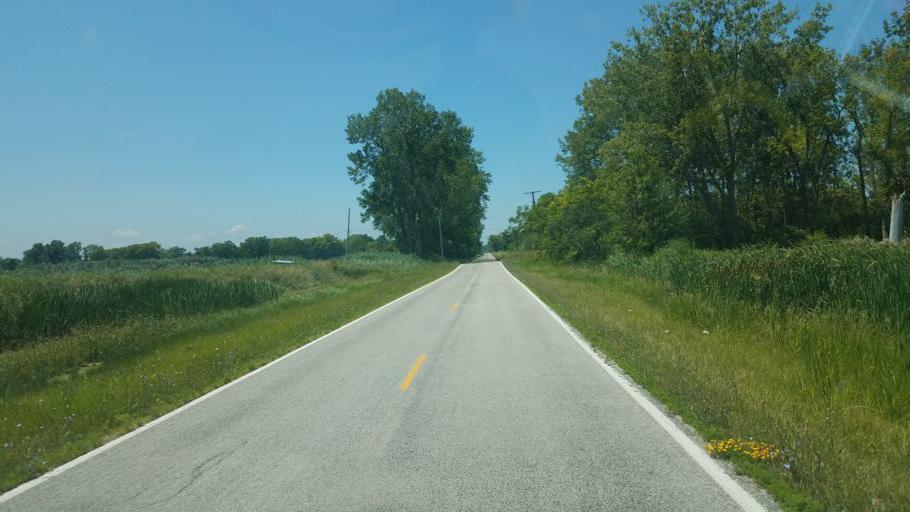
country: US
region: Ohio
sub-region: Ottawa County
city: Port Clinton
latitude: 41.4222
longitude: -83.0195
